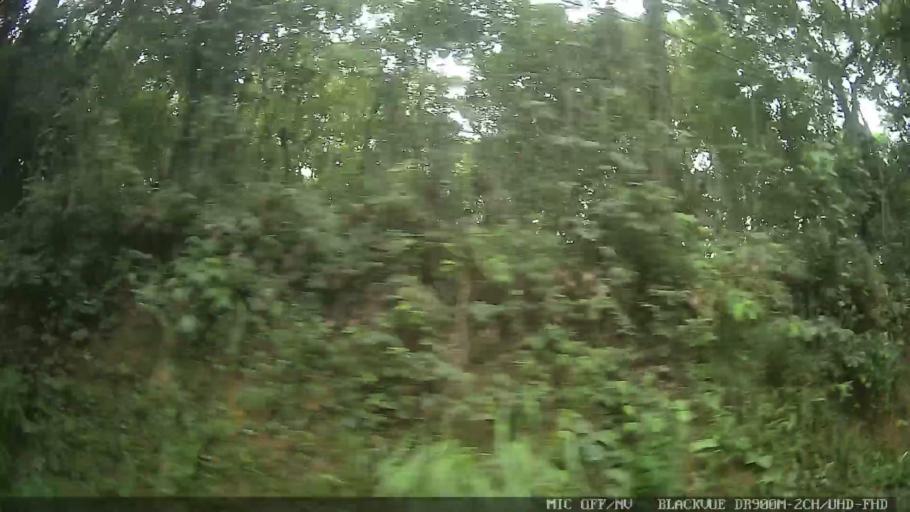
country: BR
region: Sao Paulo
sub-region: Maua
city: Maua
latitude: -23.6519
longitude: -46.4709
